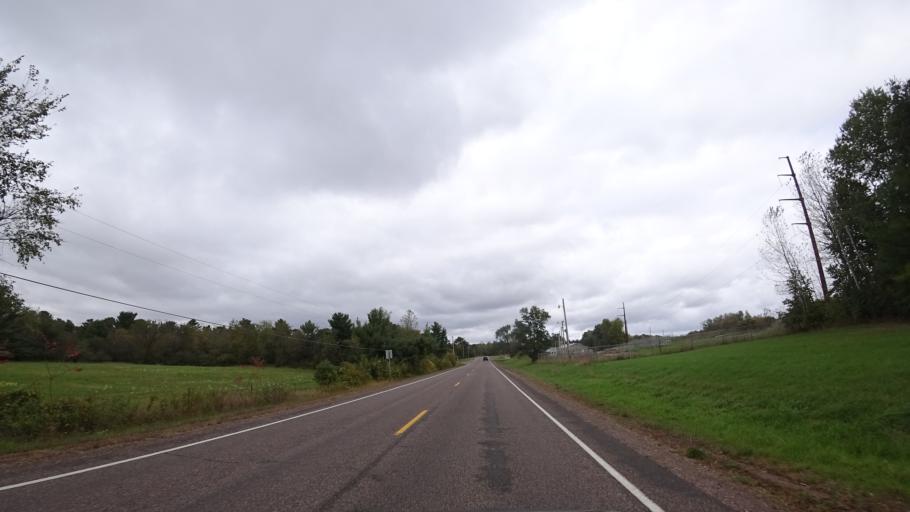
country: US
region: Wisconsin
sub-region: Chippewa County
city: Lake Wissota
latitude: 45.0271
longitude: -91.2870
